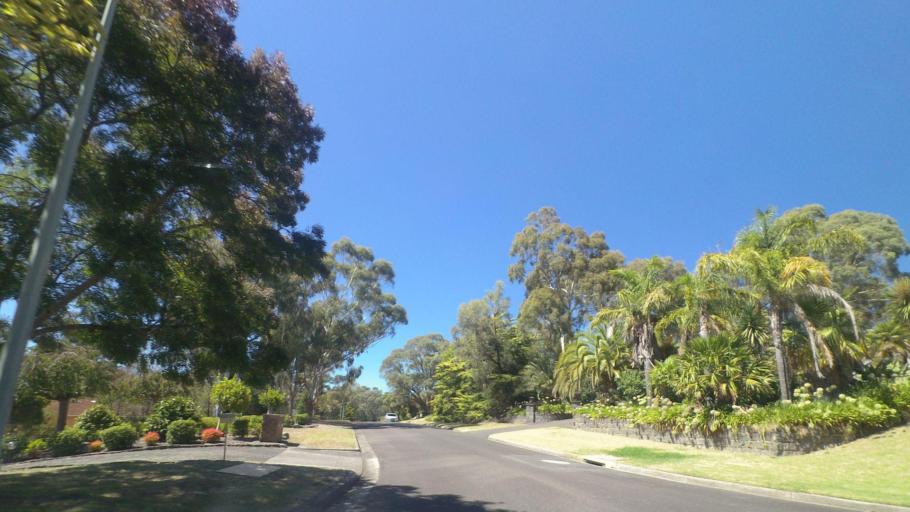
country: AU
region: Victoria
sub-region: Manningham
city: Donvale
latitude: -37.7820
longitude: 145.1904
